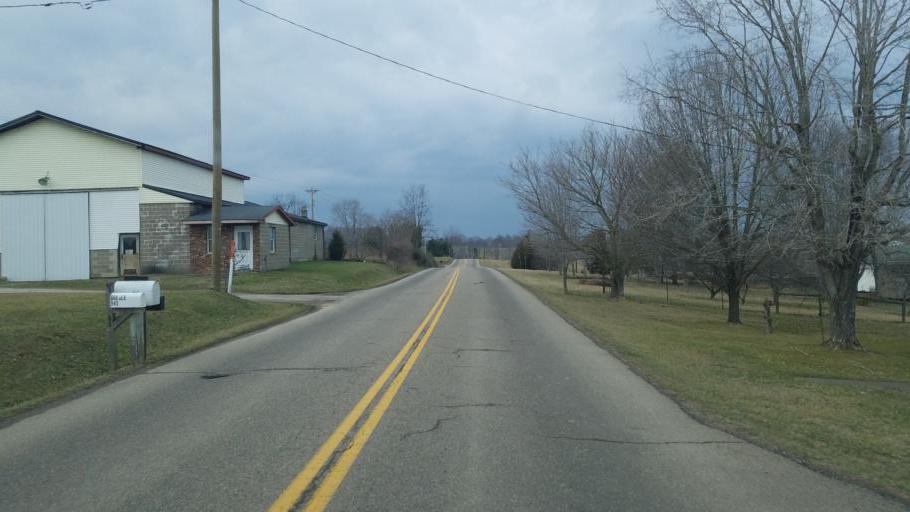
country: US
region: Ohio
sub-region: Gallia County
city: Gallipolis
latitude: 38.7829
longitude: -82.3915
